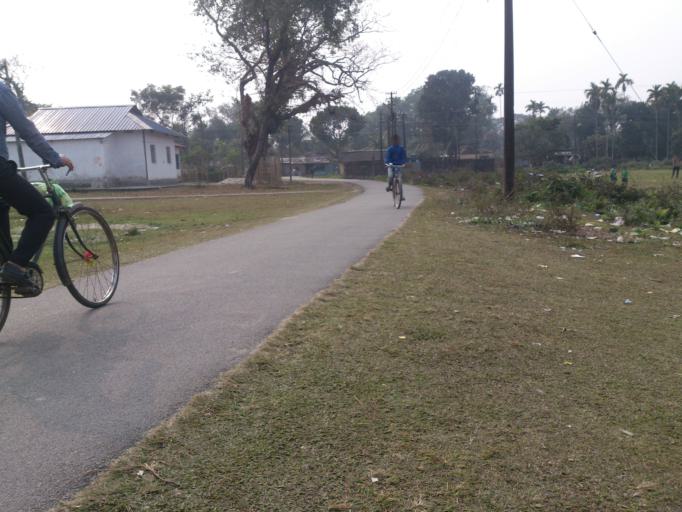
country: IN
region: Assam
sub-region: Chirang
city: Bongaigaon
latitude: 26.4788
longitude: 90.5494
